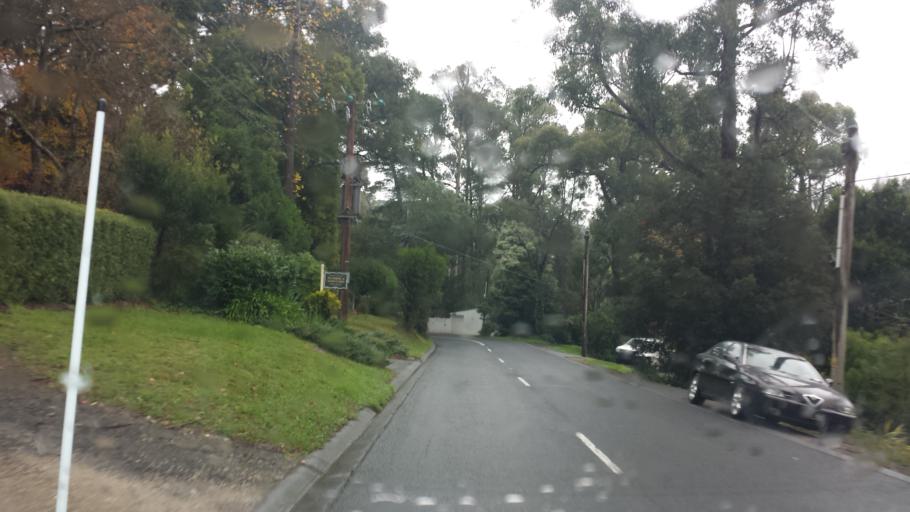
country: AU
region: Victoria
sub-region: Yarra Ranges
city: Monbulk
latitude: -37.8781
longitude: 145.4073
